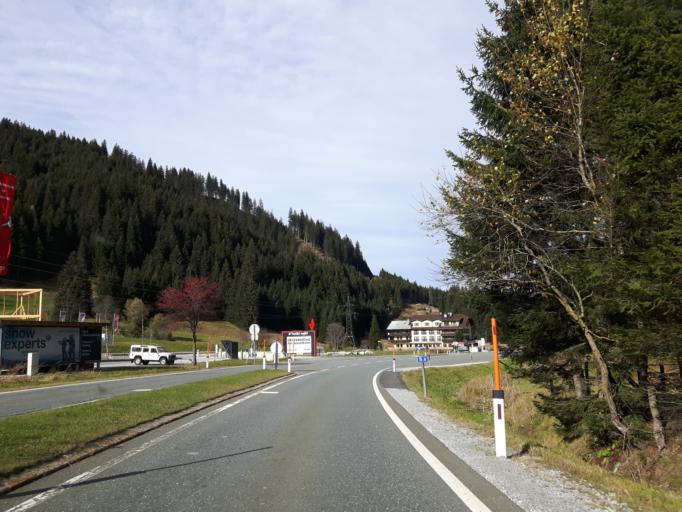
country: AT
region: Tyrol
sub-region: Politischer Bezirk Kitzbuhel
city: Jochberg
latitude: 47.3239
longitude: 12.4094
